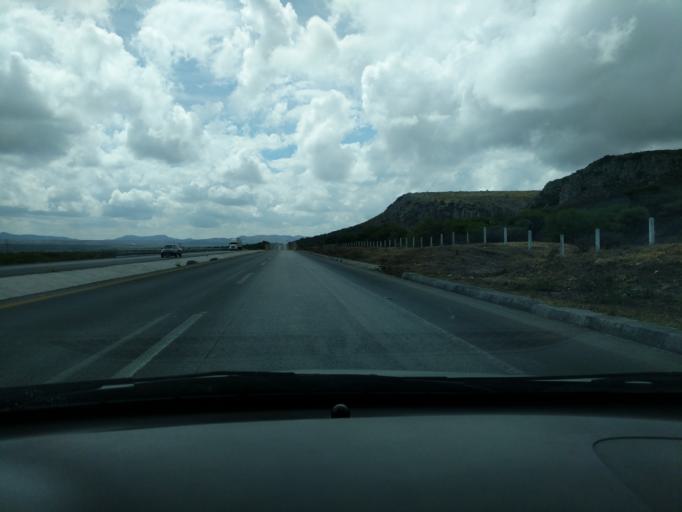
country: MX
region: Zacatecas
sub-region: Pinos
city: Santiago
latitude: 22.3998
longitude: -101.3726
